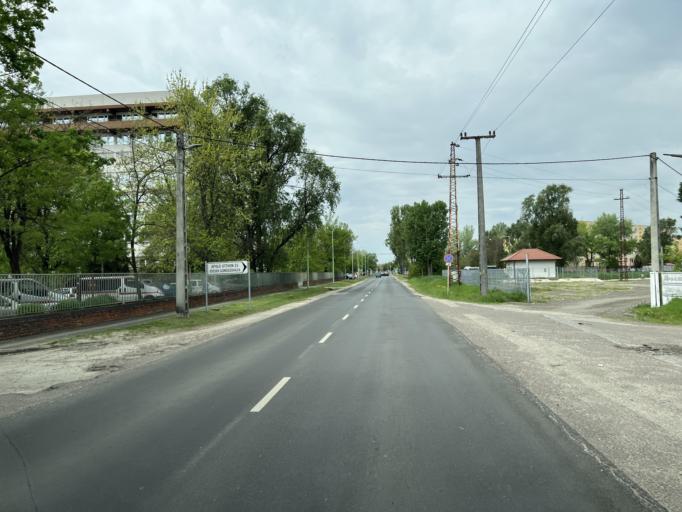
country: HU
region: Pest
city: Cegled
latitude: 47.1711
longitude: 19.8204
